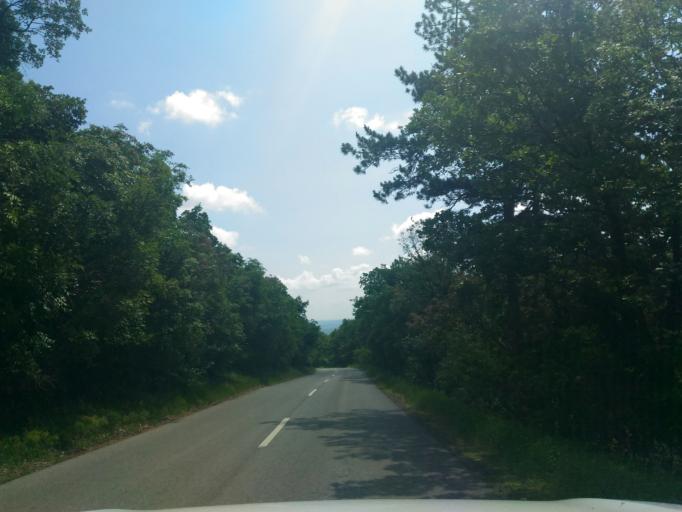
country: HU
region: Baranya
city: Pecs
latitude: 46.0978
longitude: 18.2193
